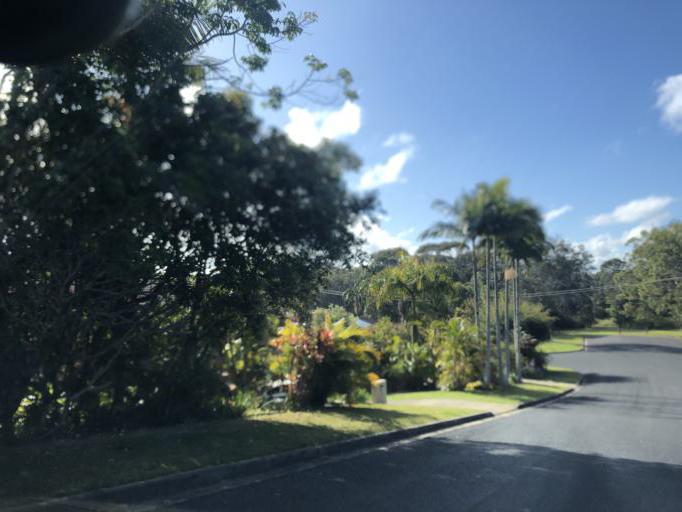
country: AU
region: New South Wales
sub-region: Coffs Harbour
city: Woolgoolga
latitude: -30.0953
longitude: 153.1987
